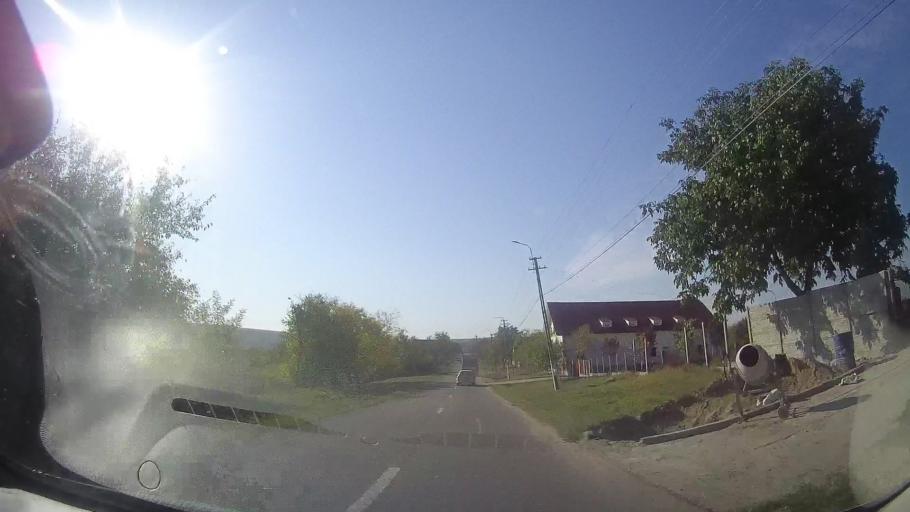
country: RO
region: Timis
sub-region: Oras Recas
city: Recas
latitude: 45.8566
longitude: 21.5157
